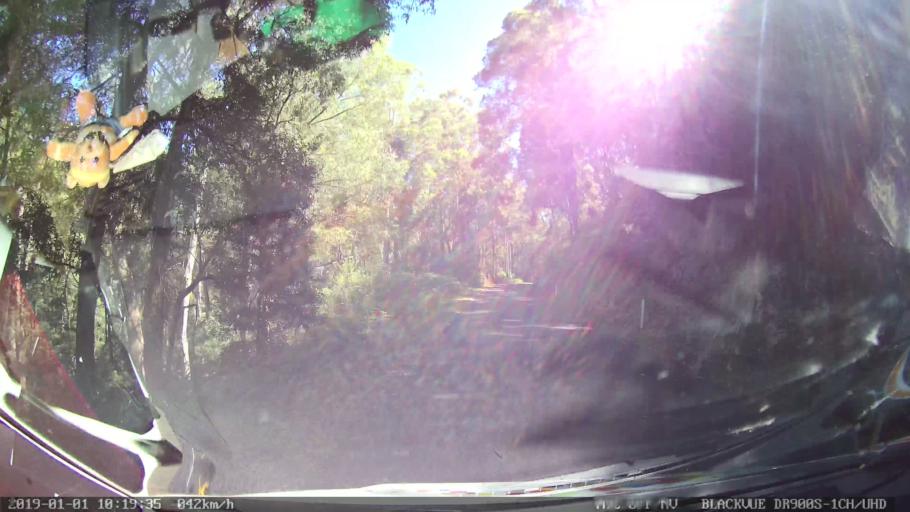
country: AU
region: New South Wales
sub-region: Snowy River
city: Jindabyne
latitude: -36.0835
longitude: 148.1859
